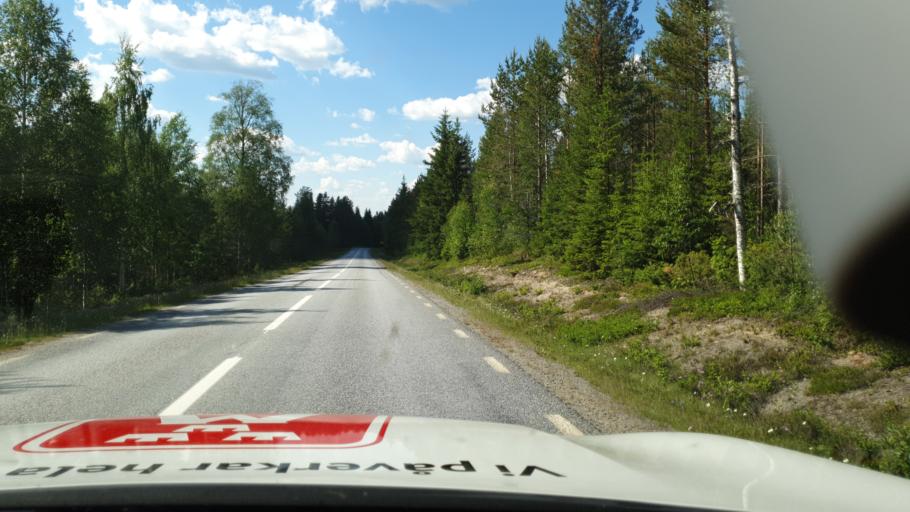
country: SE
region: Vaesterbotten
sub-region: Skelleftea Kommun
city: Burtraesk
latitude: 64.5063
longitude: 20.5029
